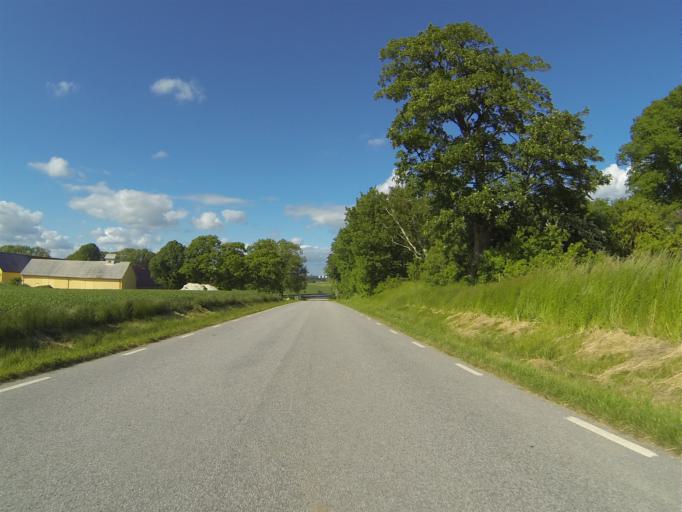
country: SE
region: Skane
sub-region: Staffanstorps Kommun
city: Hjaerup
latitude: 55.6674
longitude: 13.1702
